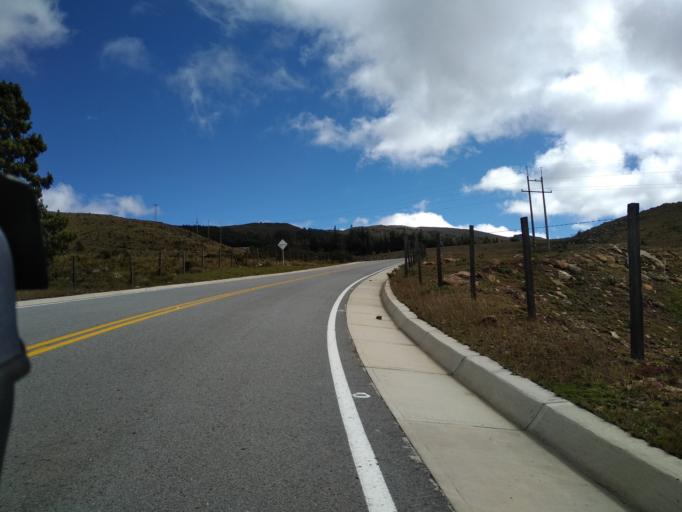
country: CO
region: Boyaca
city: Duitama
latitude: 5.9078
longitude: -73.0771
